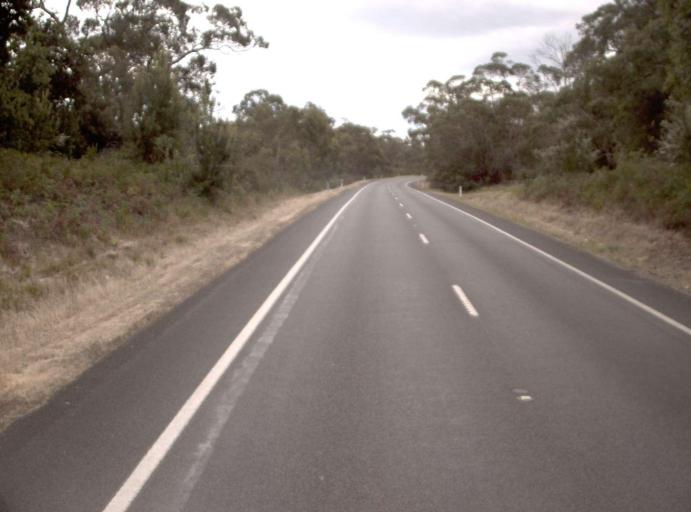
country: AU
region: Victoria
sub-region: Wellington
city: Sale
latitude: -38.2704
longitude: 147.0354
